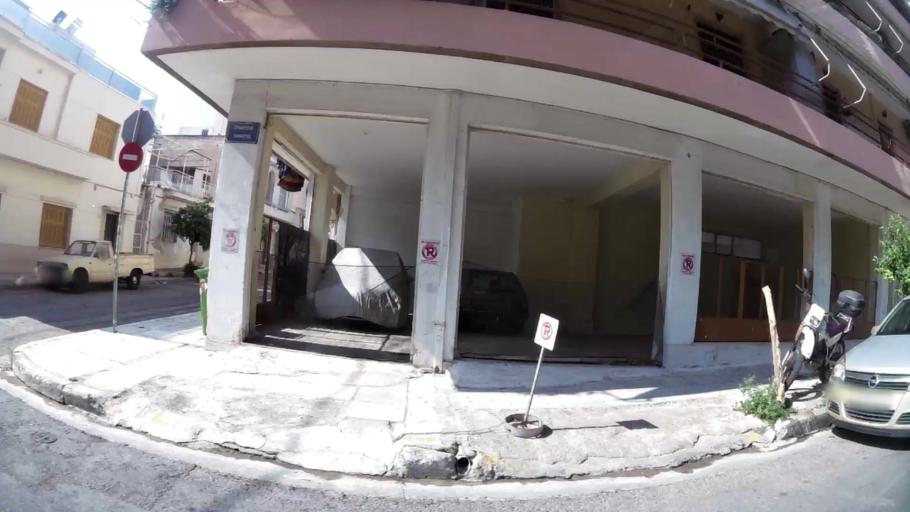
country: GR
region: Attica
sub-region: Nomos Piraios
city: Keratsini
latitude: 37.9608
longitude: 23.6311
